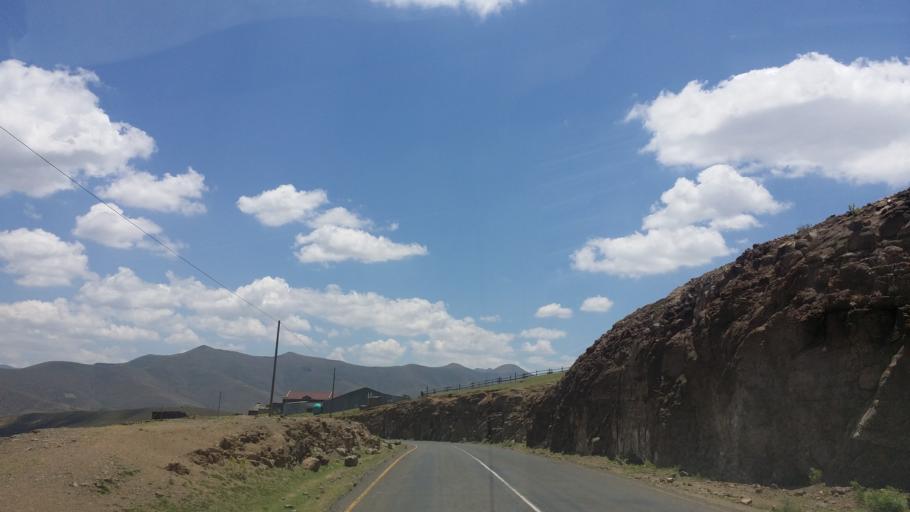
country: LS
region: Mokhotlong
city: Mokhotlong
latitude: -29.2343
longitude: 28.9086
